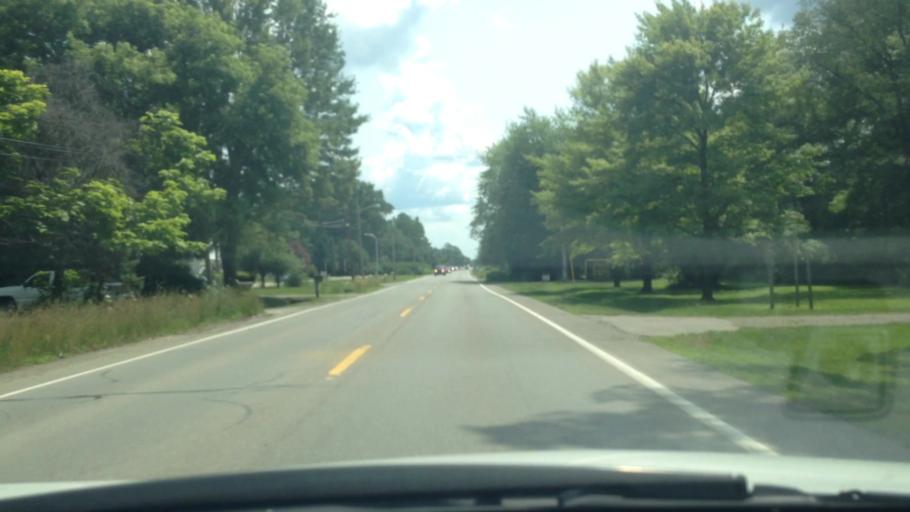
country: US
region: Michigan
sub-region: Wayne County
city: Woodhaven
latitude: 42.1747
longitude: -83.3059
